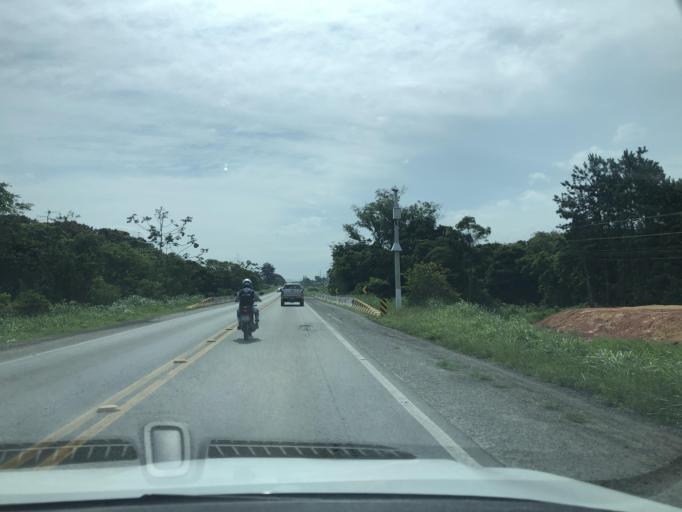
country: BR
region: Santa Catarina
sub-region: Sao Francisco Do Sul
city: Sao Francisco do Sul
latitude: -26.3709
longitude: -48.7002
